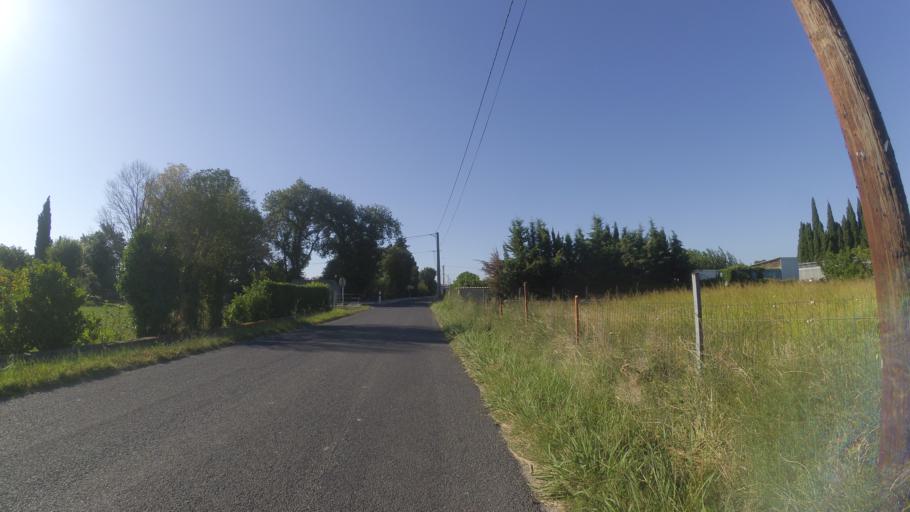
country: FR
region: Languedoc-Roussillon
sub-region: Departement des Pyrenees-Orientales
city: Villeneuve-la-Riviere
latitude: 42.6993
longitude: 2.7996
